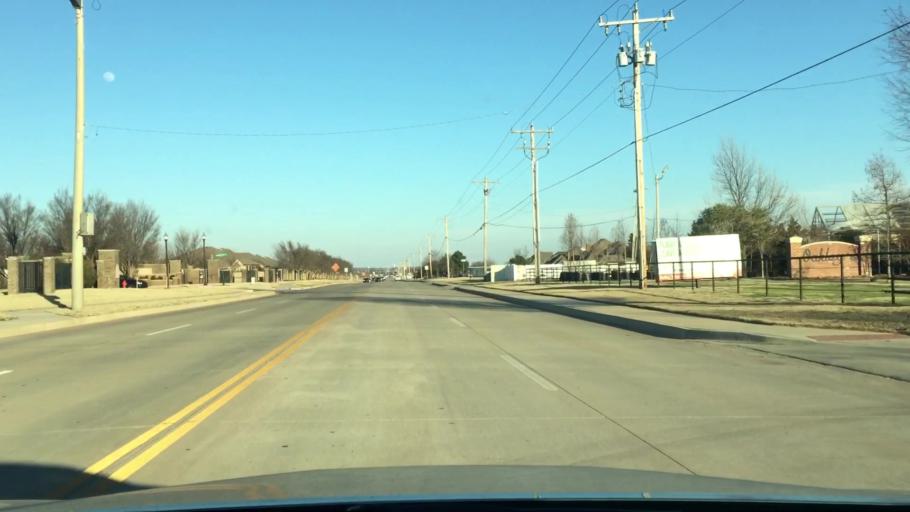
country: US
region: Oklahoma
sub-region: Oklahoma County
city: Edmond
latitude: 35.6531
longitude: -97.5638
